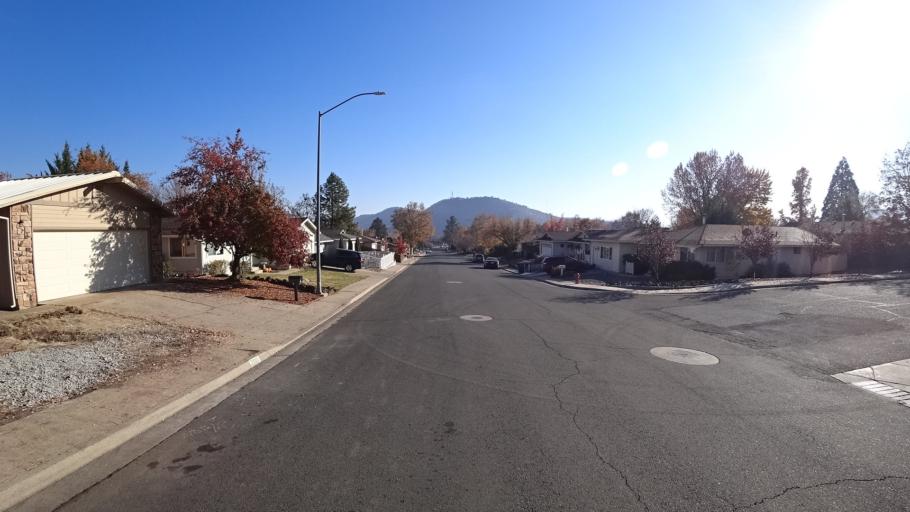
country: US
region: California
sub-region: Siskiyou County
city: Yreka
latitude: 41.7227
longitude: -122.6489
